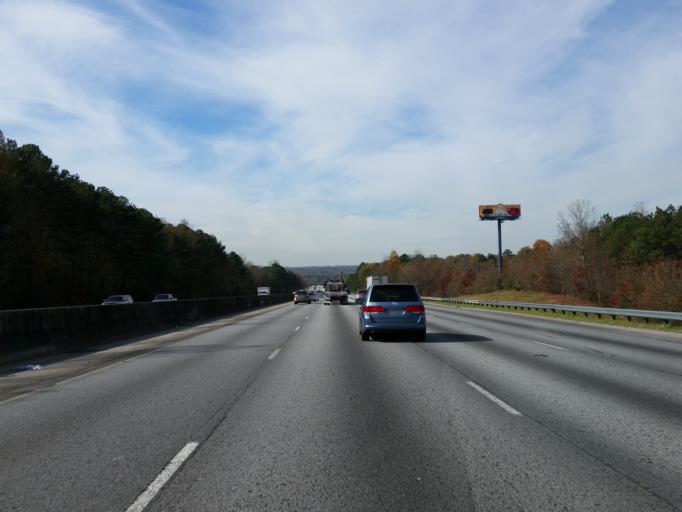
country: US
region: Georgia
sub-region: Cobb County
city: Mableton
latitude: 33.7760
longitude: -84.5903
